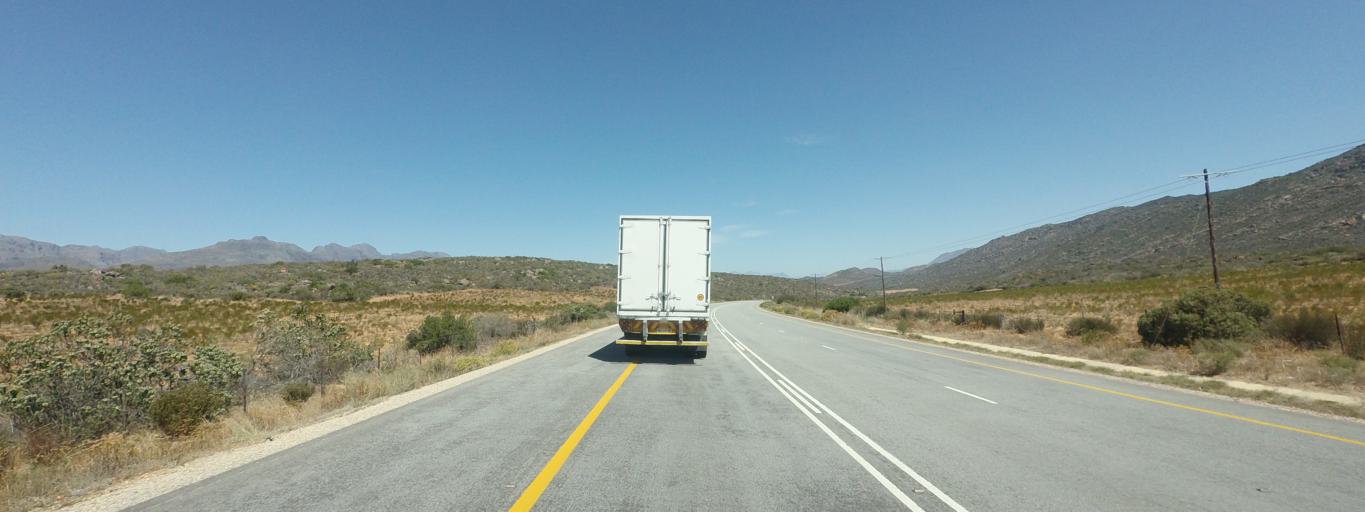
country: ZA
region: Western Cape
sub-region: West Coast District Municipality
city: Clanwilliam
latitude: -32.3284
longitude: 18.9231
